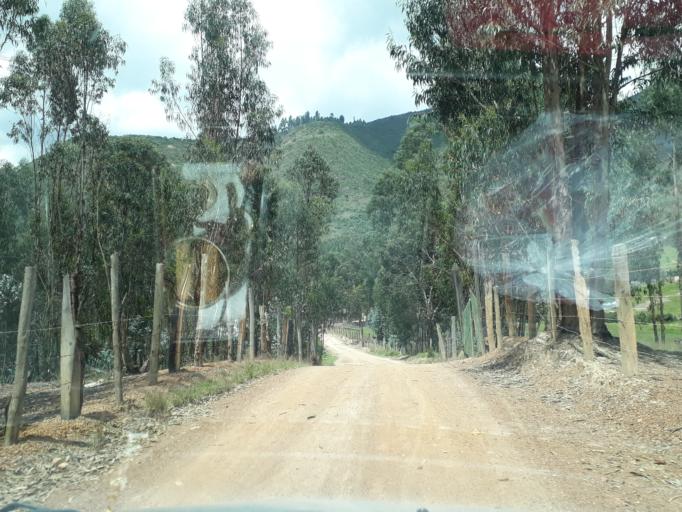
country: CO
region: Boyaca
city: Floresta
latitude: 5.8512
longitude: -72.9515
